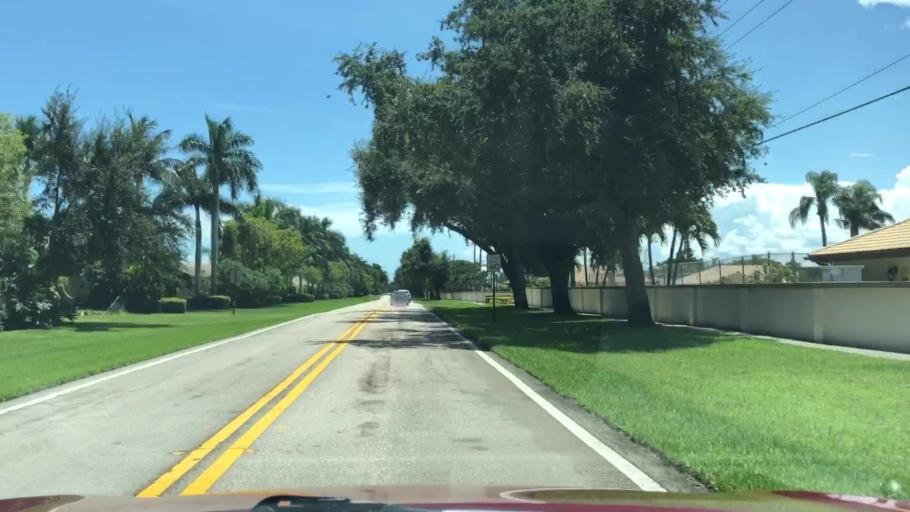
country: US
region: Florida
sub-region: Palm Beach County
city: Boynton Beach
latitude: 26.5211
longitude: -80.1066
